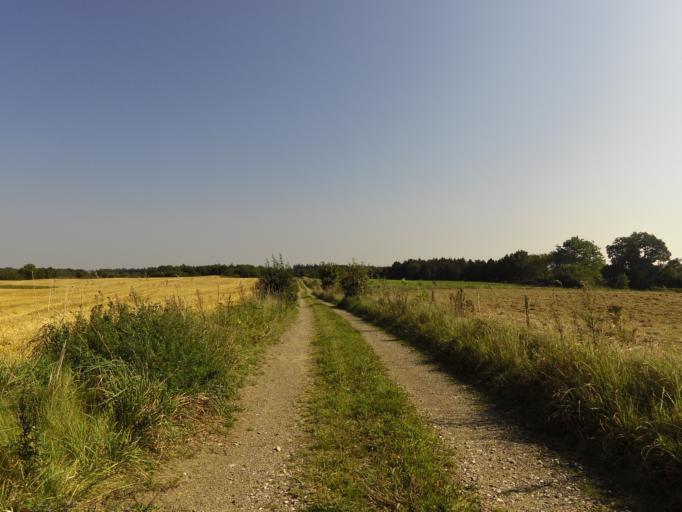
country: DK
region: South Denmark
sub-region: Aabenraa Kommune
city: Krusa
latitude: 54.9341
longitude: 9.4573
